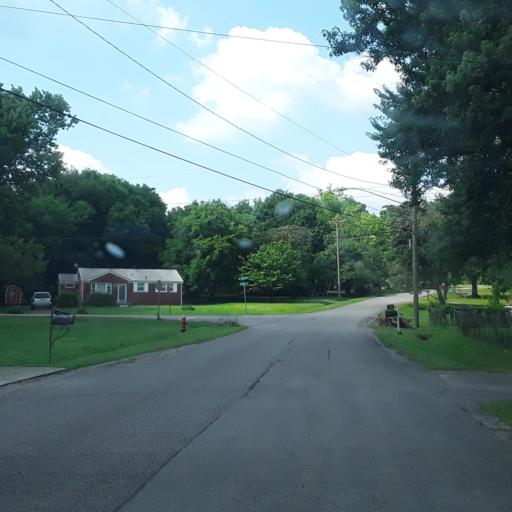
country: US
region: Tennessee
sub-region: Davidson County
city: Oak Hill
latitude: 36.1159
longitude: -86.7264
